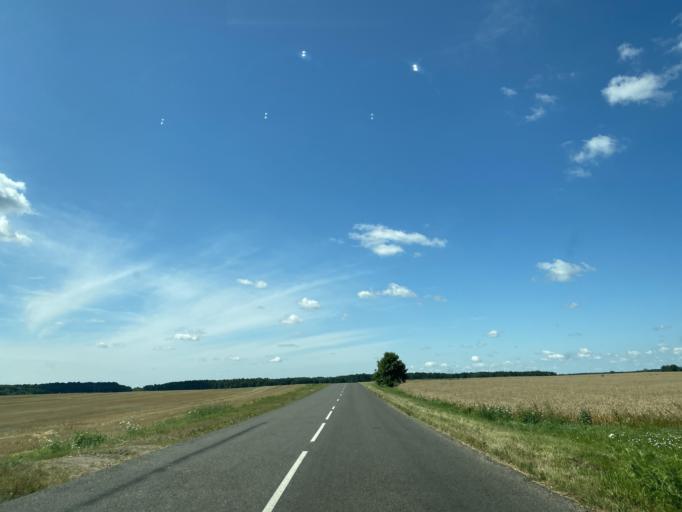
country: BY
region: Brest
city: Ivanava
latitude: 52.2322
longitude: 25.6503
